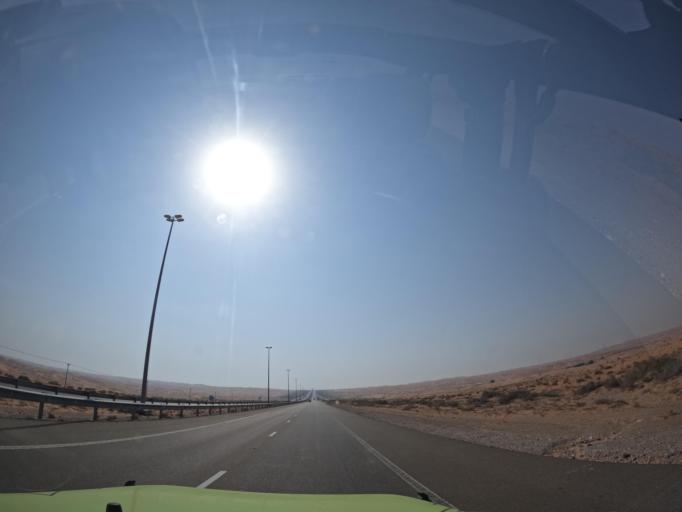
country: OM
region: Al Buraimi
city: Al Buraymi
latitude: 24.4431
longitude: 55.6618
